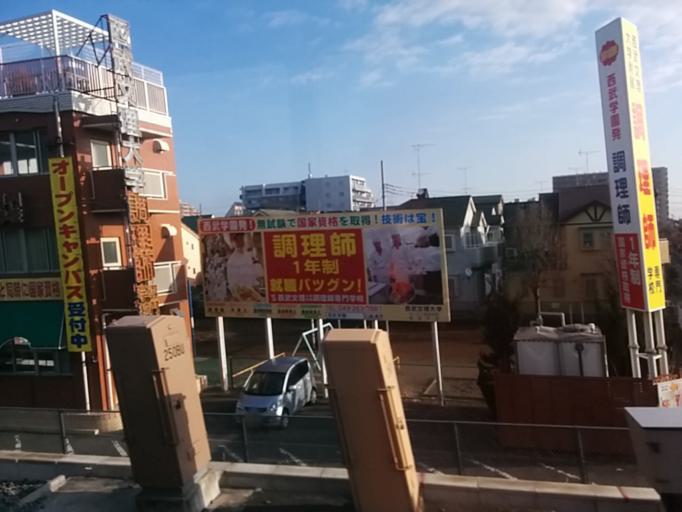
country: JP
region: Saitama
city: Kamifukuoka
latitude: 35.8673
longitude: 139.5175
